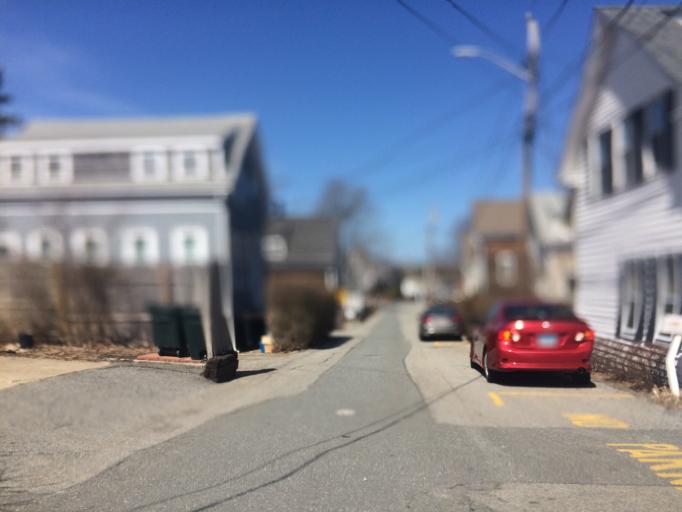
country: US
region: Massachusetts
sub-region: Barnstable County
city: Provincetown
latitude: 42.0472
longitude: -70.1928
